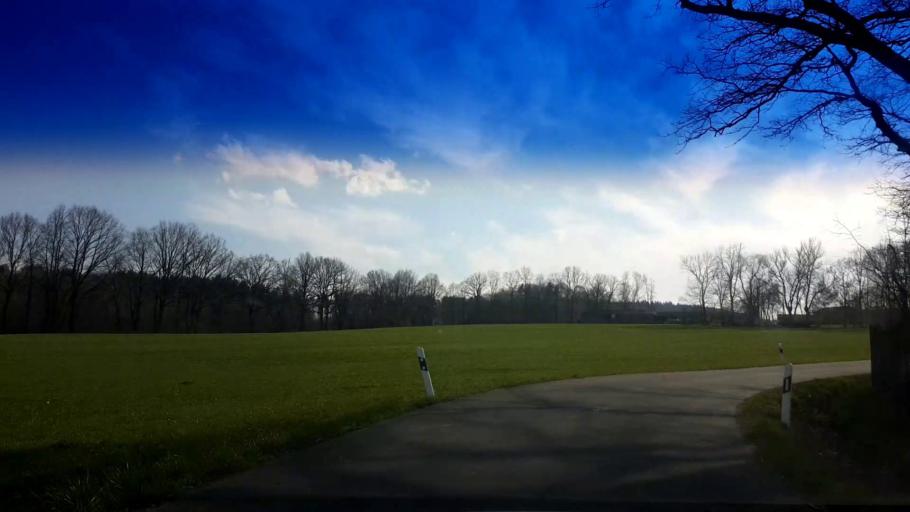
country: DE
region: Bavaria
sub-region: Upper Franconia
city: Gesees
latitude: 50.0291
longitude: 11.6228
